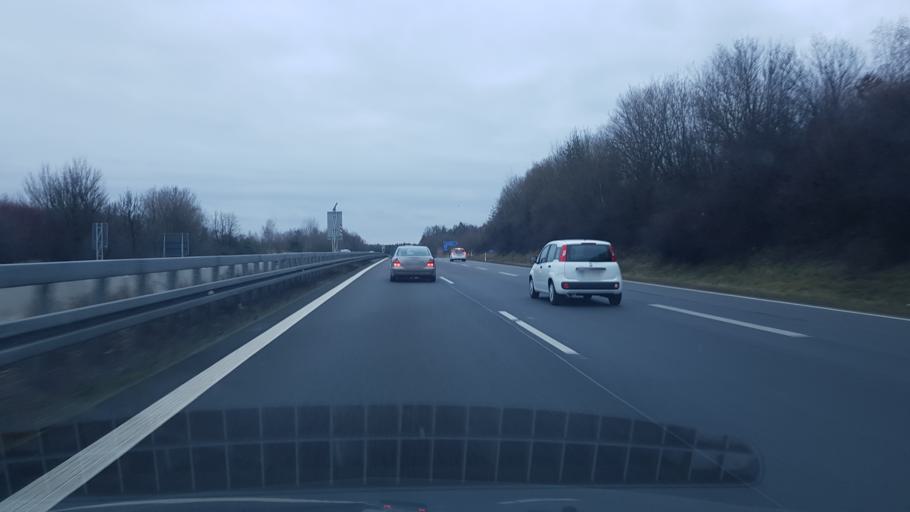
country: DE
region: Saxony
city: Ohorn
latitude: 51.1643
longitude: 14.0508
